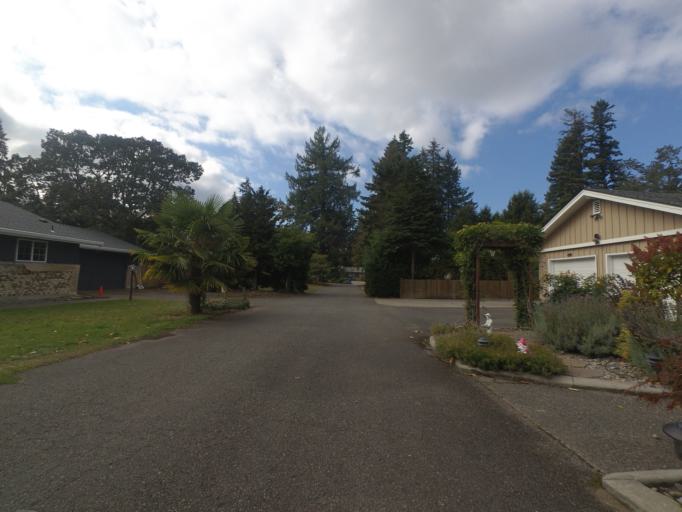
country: US
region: Washington
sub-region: Pierce County
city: Lakewood
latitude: 47.1690
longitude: -122.5453
